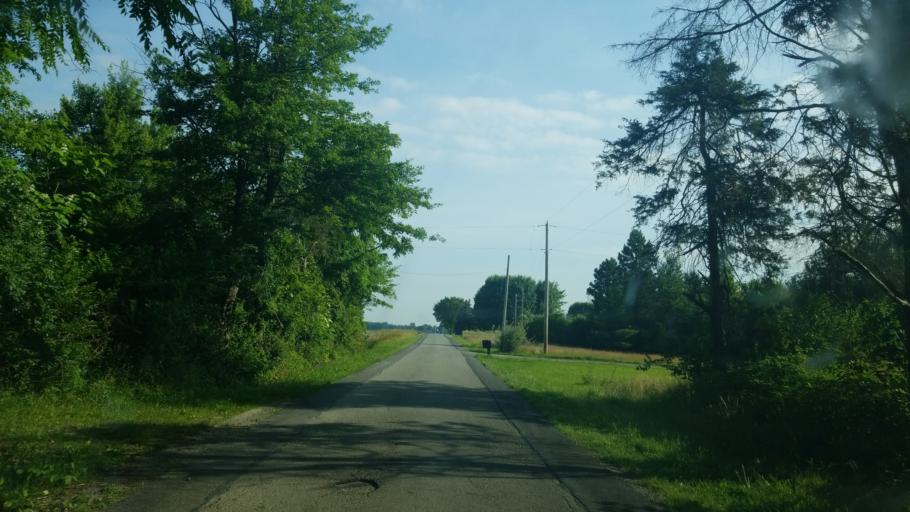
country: US
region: Ohio
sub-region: Hancock County
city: Arlington
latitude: 40.8230
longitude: -83.6705
